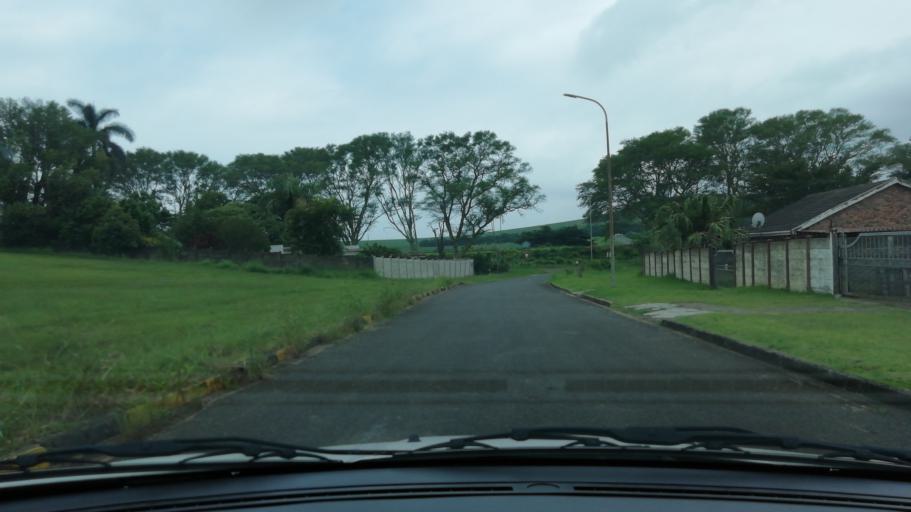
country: ZA
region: KwaZulu-Natal
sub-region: uThungulu District Municipality
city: Empangeni
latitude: -28.7390
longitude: 31.9014
